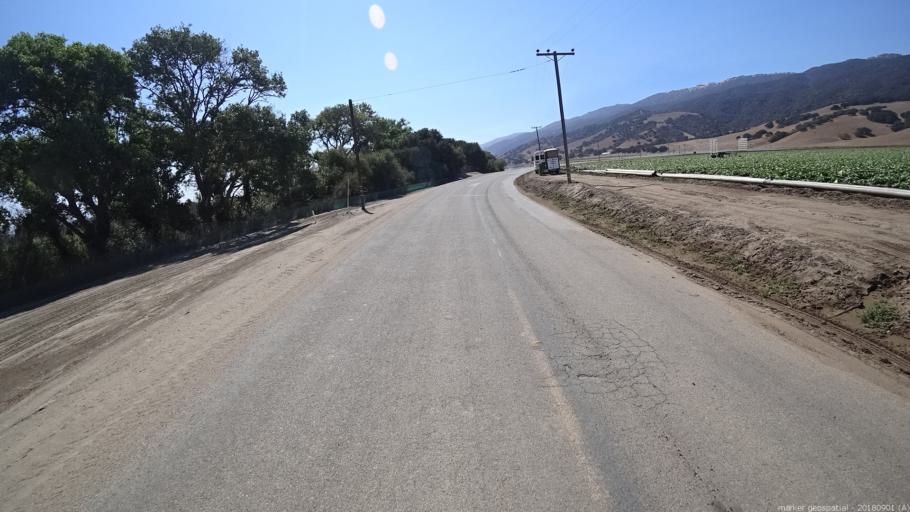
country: US
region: California
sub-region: Monterey County
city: Chualar
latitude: 36.5409
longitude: -121.5415
